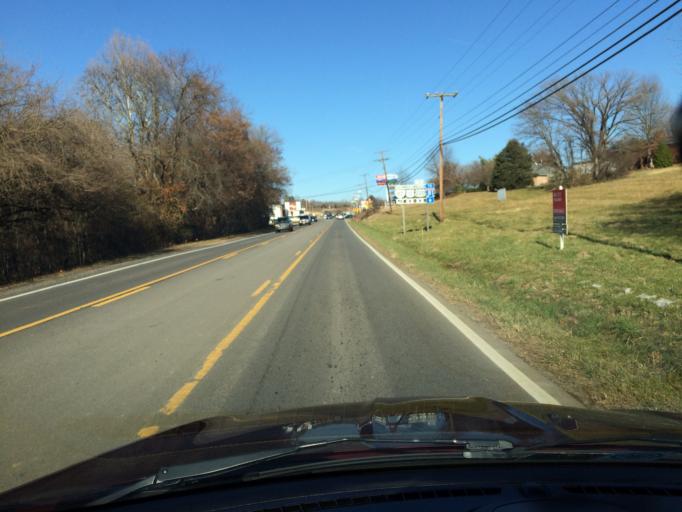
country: US
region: Virginia
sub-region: Roanoke County
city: Hollins
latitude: 37.3414
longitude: -79.9563
